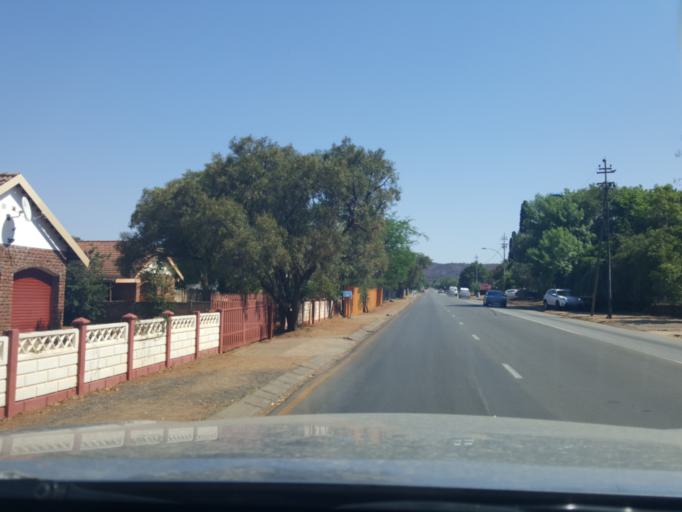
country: ZA
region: North-West
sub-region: Ngaka Modiri Molema District Municipality
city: Zeerust
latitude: -25.5365
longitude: 26.0770
